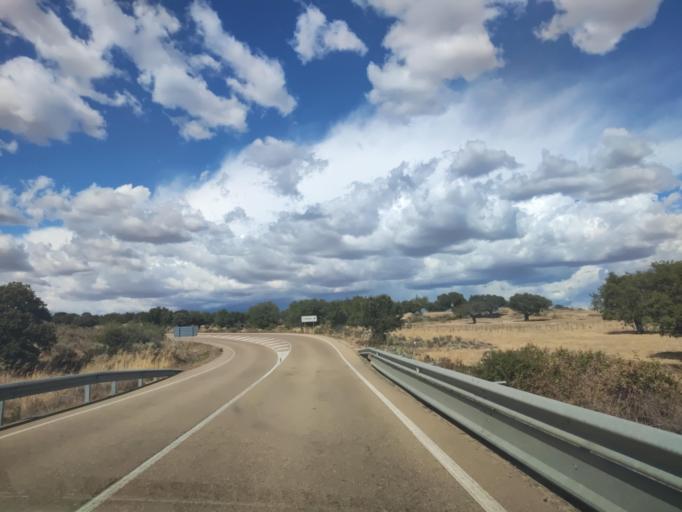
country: ES
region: Castille and Leon
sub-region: Provincia de Salamanca
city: Buenamadre
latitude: 40.8989
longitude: -6.3210
